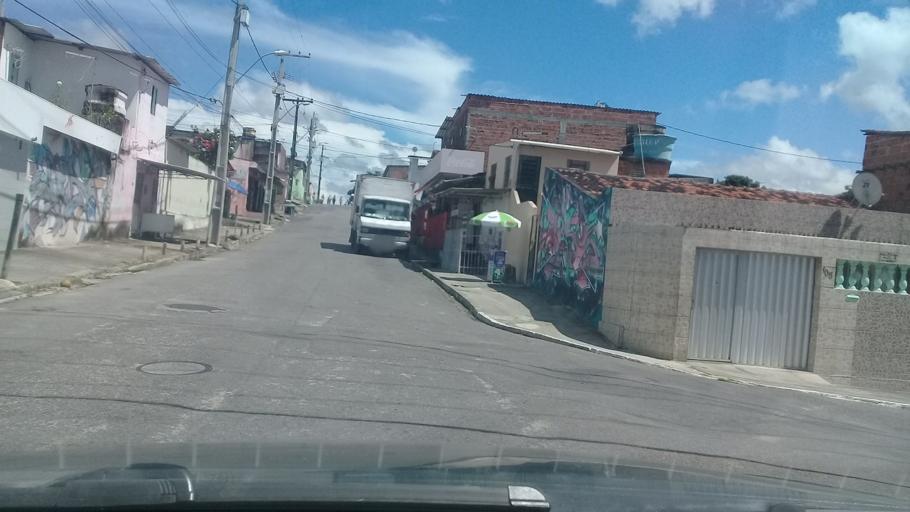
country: BR
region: Pernambuco
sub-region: Jaboatao Dos Guararapes
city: Jaboatao dos Guararapes
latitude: -8.1289
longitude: -34.9469
